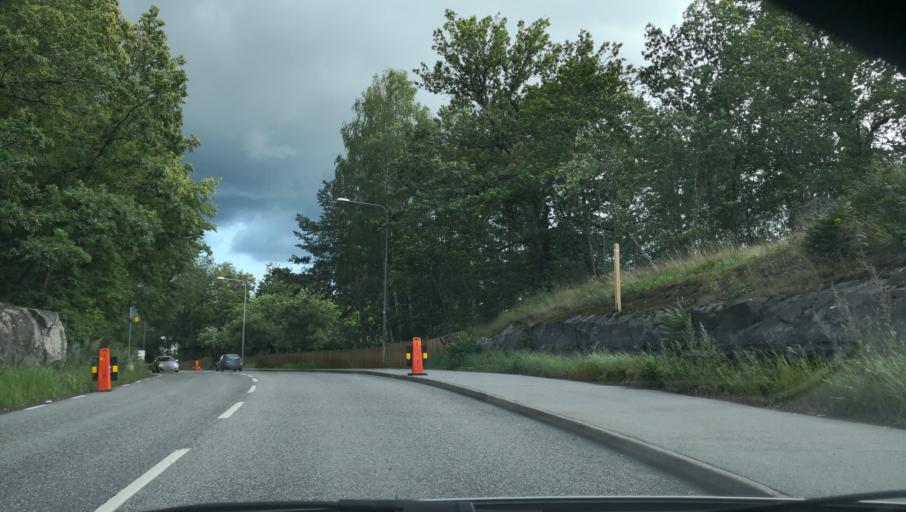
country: SE
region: Stockholm
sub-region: Stockholms Kommun
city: Arsta
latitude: 59.2524
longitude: 18.0495
